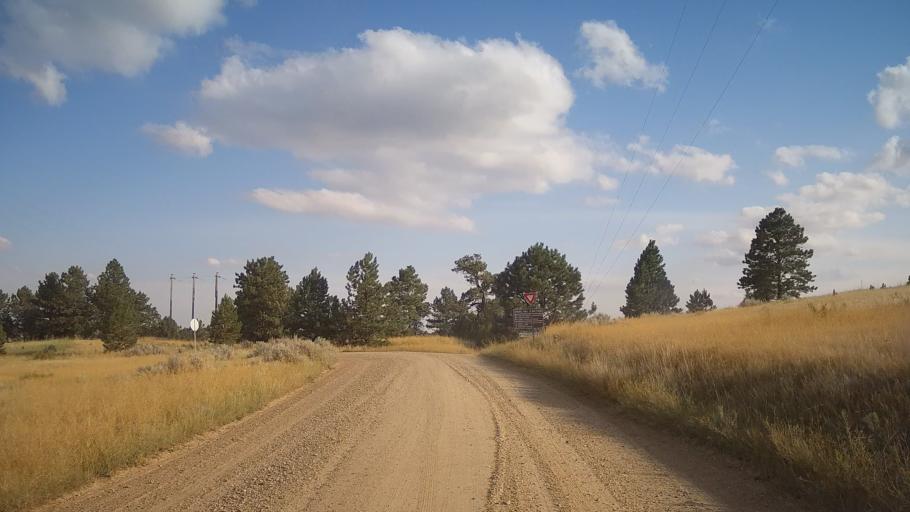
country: US
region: Montana
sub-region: Dawson County
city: Glendive
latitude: 47.0520
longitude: -104.6772
